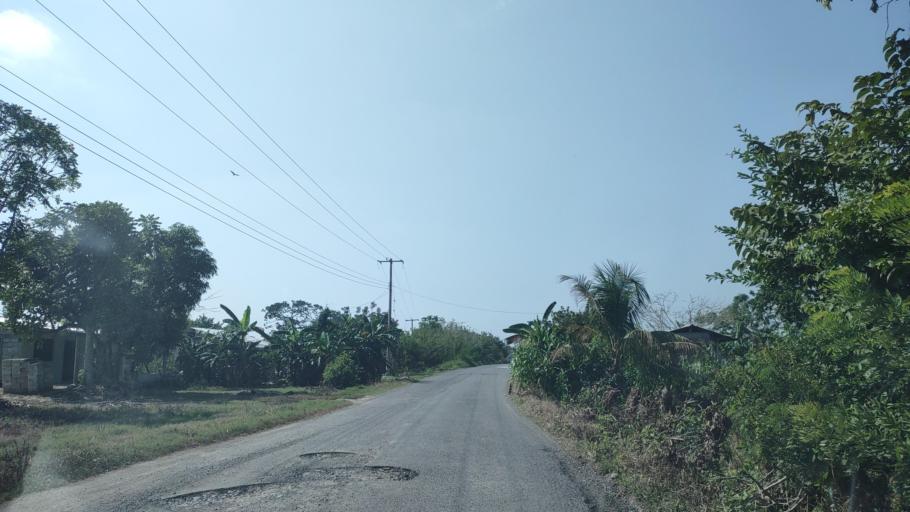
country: MX
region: Puebla
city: Espinal
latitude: 20.2587
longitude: -97.3196
